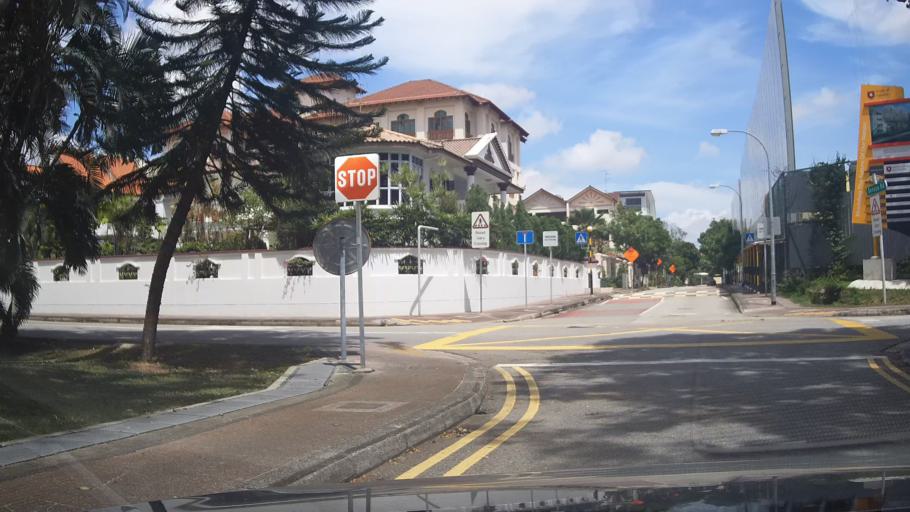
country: SG
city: Singapore
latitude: 1.3054
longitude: 103.8993
